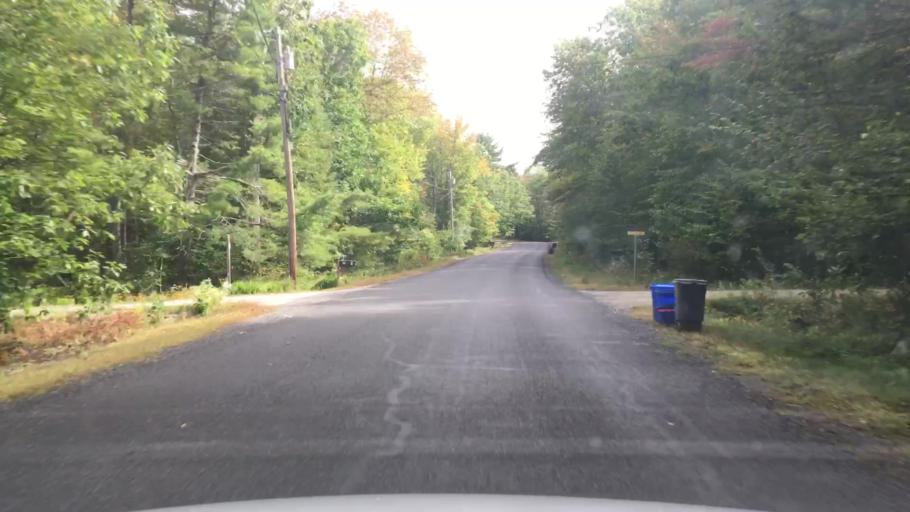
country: US
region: Maine
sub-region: Androscoggin County
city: Lisbon Falls
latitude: 43.9596
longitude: -70.0532
